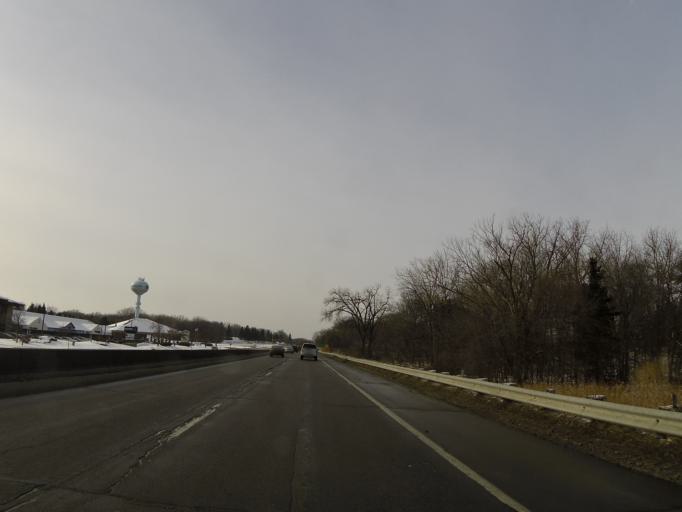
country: US
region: Minnesota
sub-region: Hennepin County
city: Deephaven
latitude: 44.9091
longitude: -93.5294
